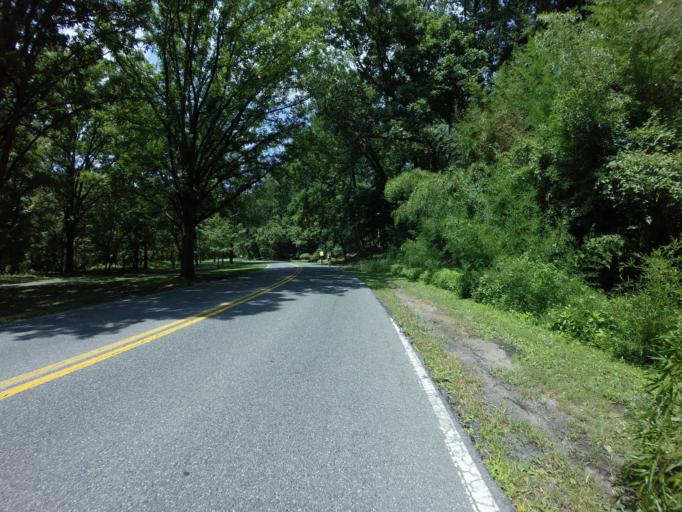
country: US
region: Maryland
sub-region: Montgomery County
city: South Kensington
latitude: 39.0088
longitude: -77.0829
